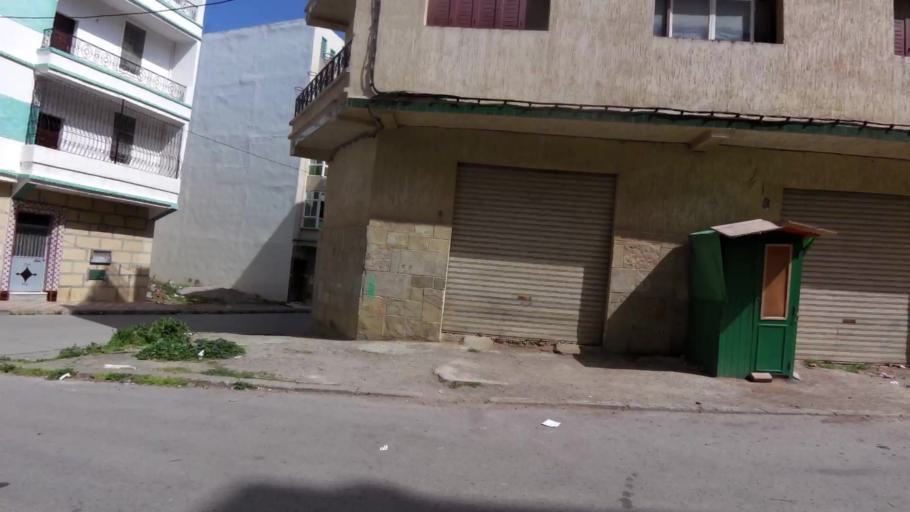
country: MA
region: Tanger-Tetouan
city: Tetouan
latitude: 35.5881
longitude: -5.3535
